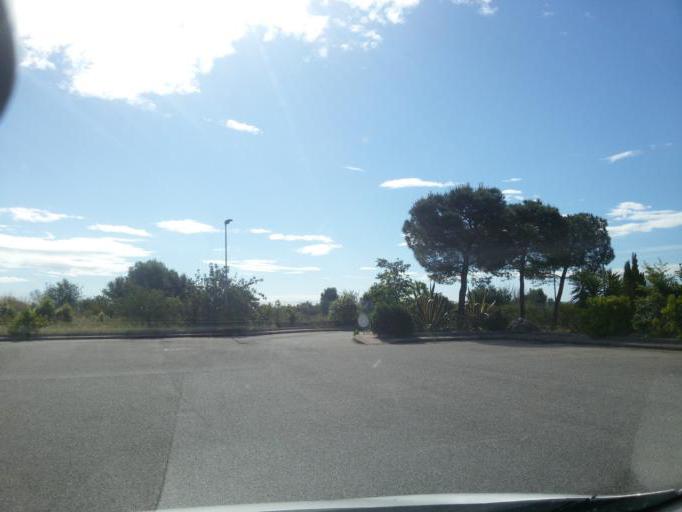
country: IT
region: Apulia
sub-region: Provincia di Taranto
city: Paolo VI
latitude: 40.5269
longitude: 17.2842
